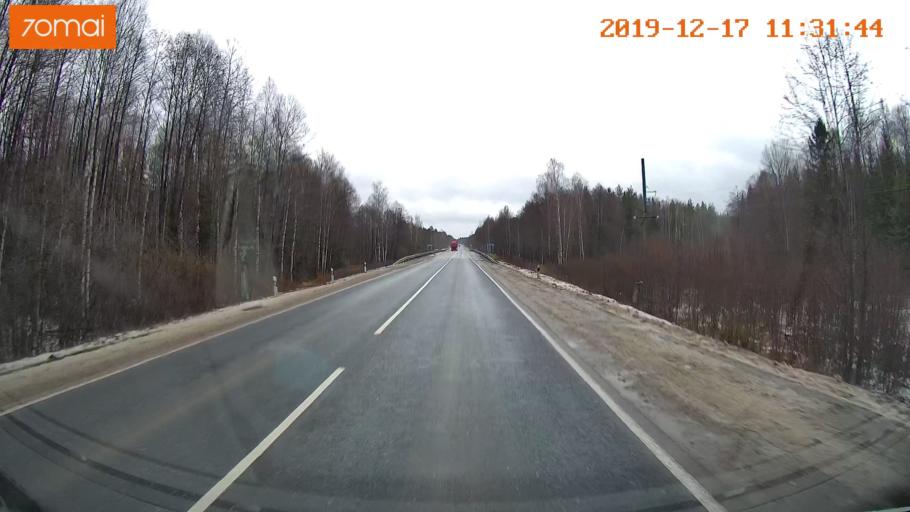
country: RU
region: Vladimir
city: Kurlovo
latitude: 55.4300
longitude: 40.6361
